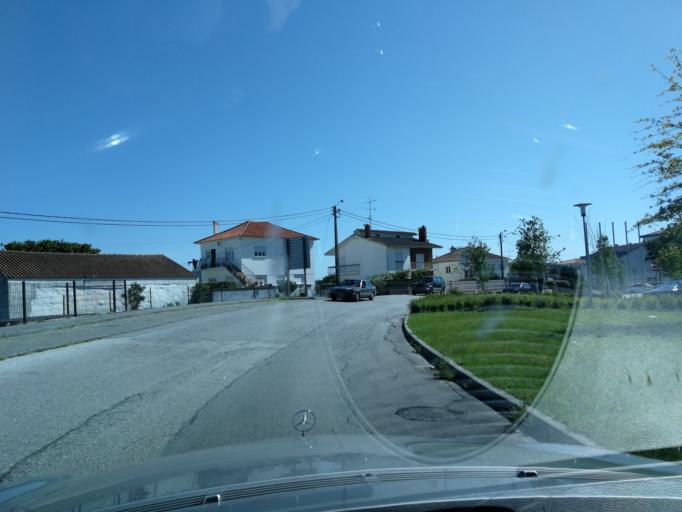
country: PT
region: Viana do Castelo
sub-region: Viana do Castelo
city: Meadela
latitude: 41.7097
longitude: -8.8025
